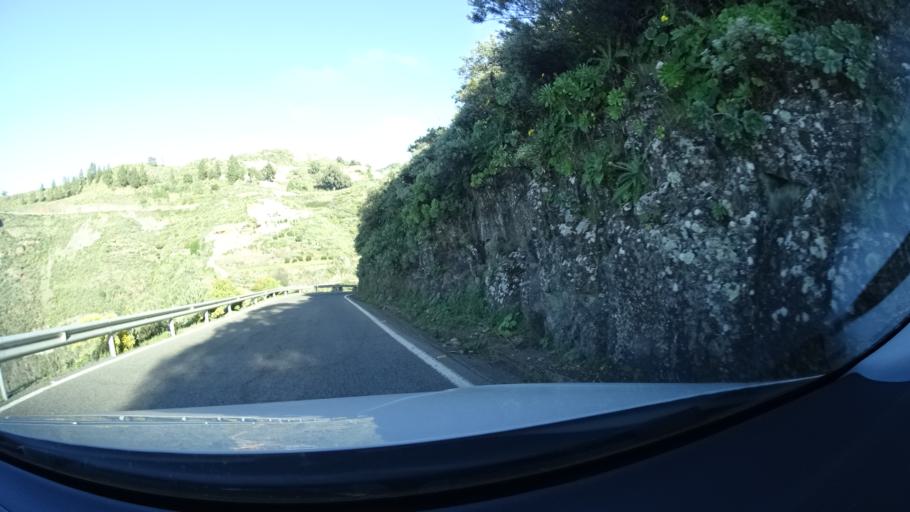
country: ES
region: Canary Islands
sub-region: Provincia de Las Palmas
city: Artenara
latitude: 28.0396
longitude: -15.6462
